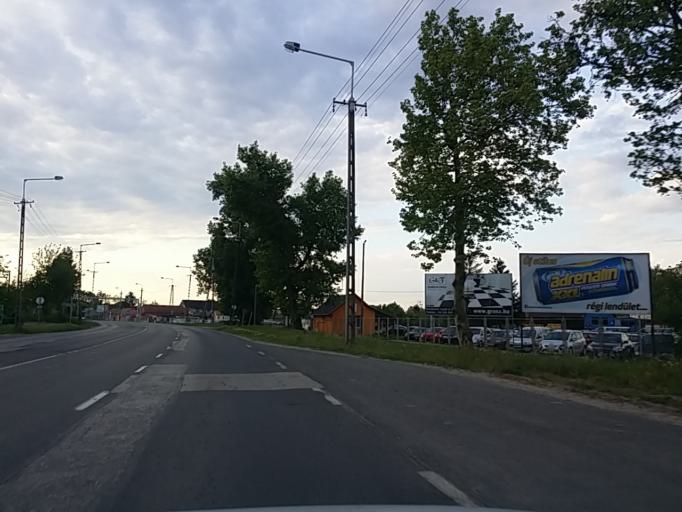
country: HU
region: Bacs-Kiskun
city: Kecskemet
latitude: 46.9280
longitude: 19.6651
